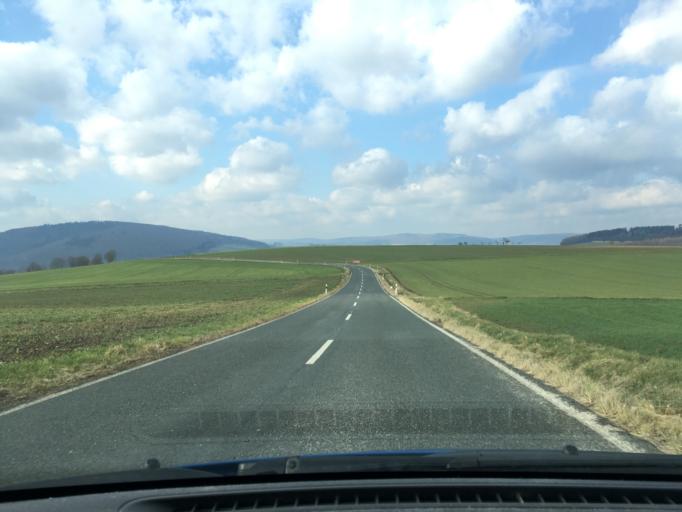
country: DE
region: Lower Saxony
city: Uslar
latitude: 51.6137
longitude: 9.6313
